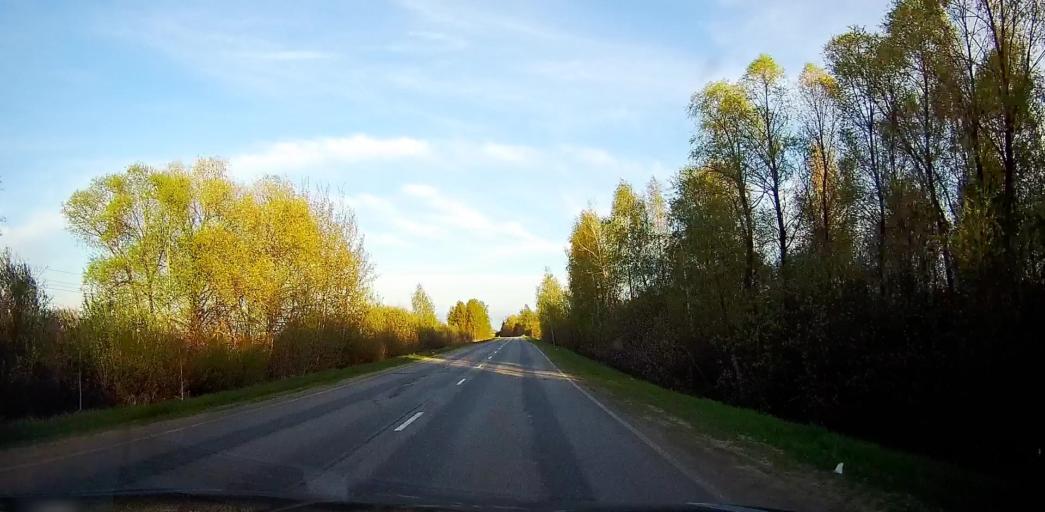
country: RU
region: Moskovskaya
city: Bronnitsy
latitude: 55.2766
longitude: 38.2233
